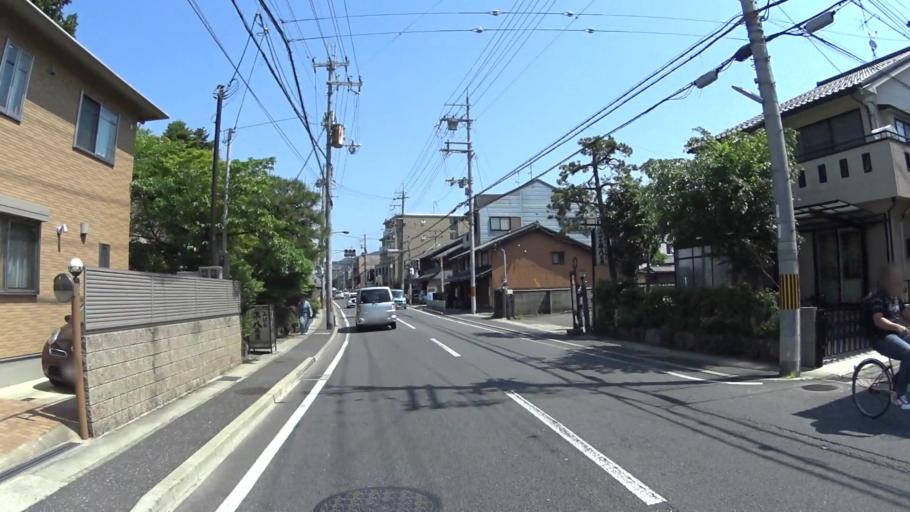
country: JP
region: Kyoto
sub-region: Kyoto-shi
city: Kamigyo-ku
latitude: 35.0531
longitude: 135.7909
